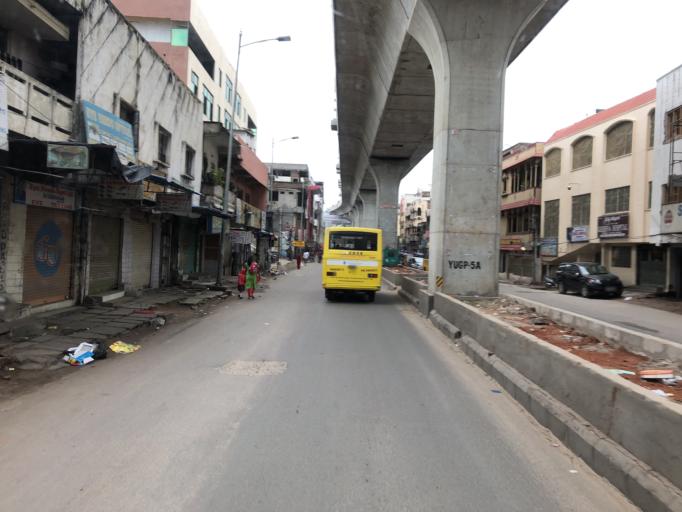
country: IN
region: Telangana
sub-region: Rangareddi
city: Kukatpalli
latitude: 17.4338
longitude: 78.4268
